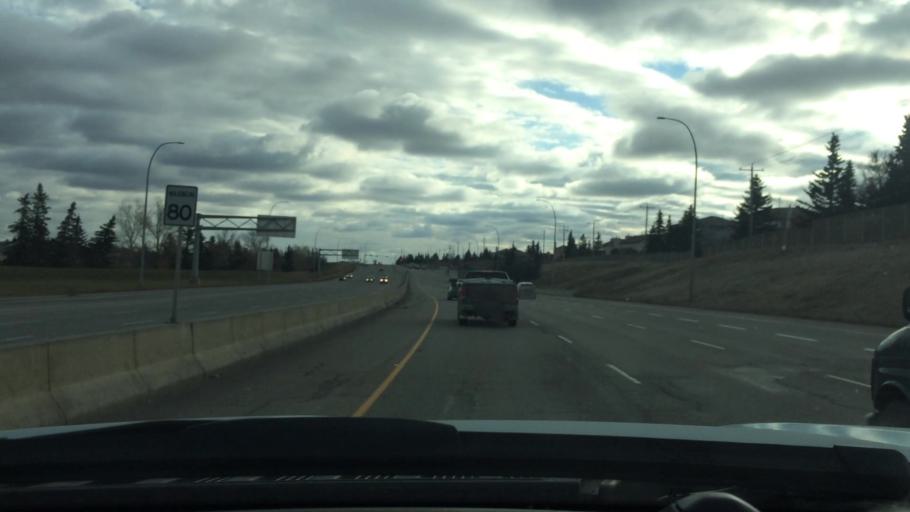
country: CA
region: Alberta
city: Calgary
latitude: 51.1409
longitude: -114.0886
